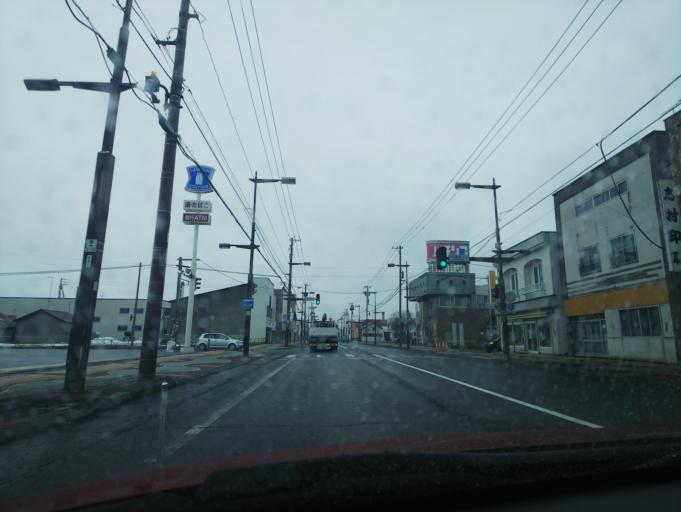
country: JP
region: Hokkaido
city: Nayoro
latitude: 44.1780
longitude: 142.3916
